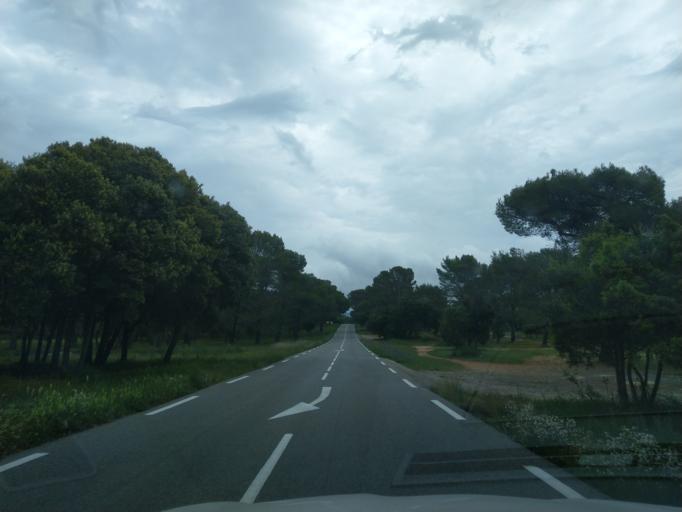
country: FR
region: Provence-Alpes-Cote d'Azur
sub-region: Departement du Var
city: Le Castellet
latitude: 43.2628
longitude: 5.7624
